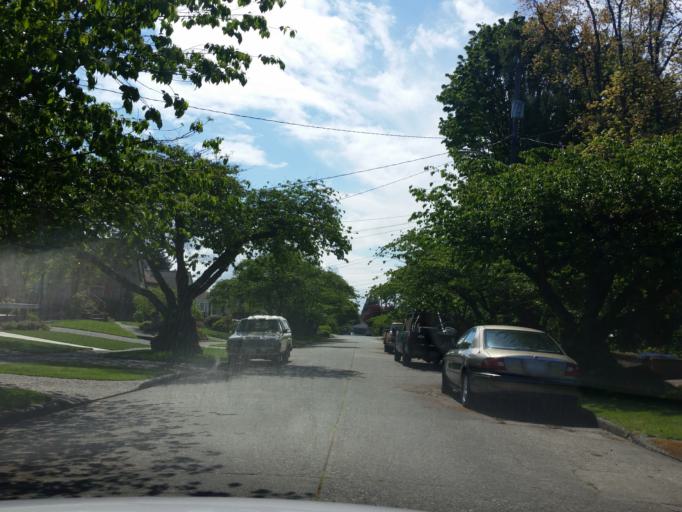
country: US
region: Washington
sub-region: King County
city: Shoreline
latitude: 47.6861
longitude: -122.3994
